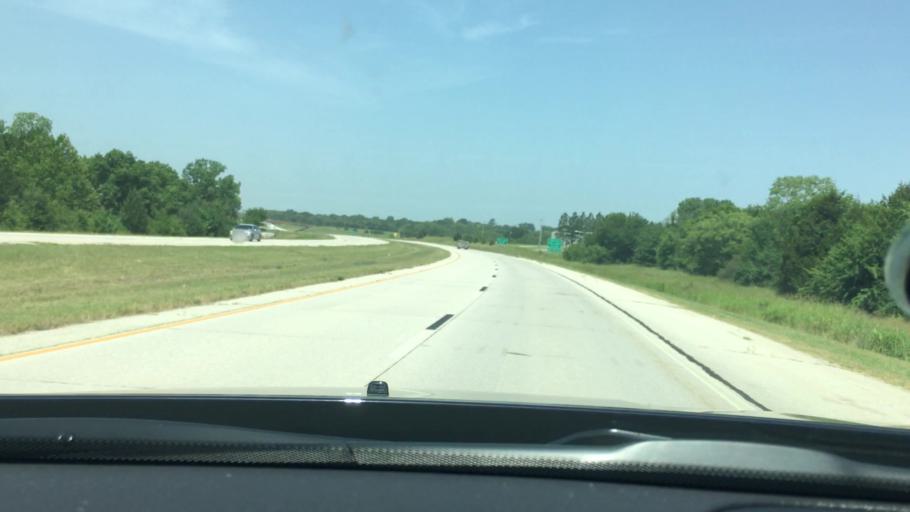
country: US
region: Oklahoma
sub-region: Pontotoc County
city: Ada
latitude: 34.7516
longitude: -96.6613
